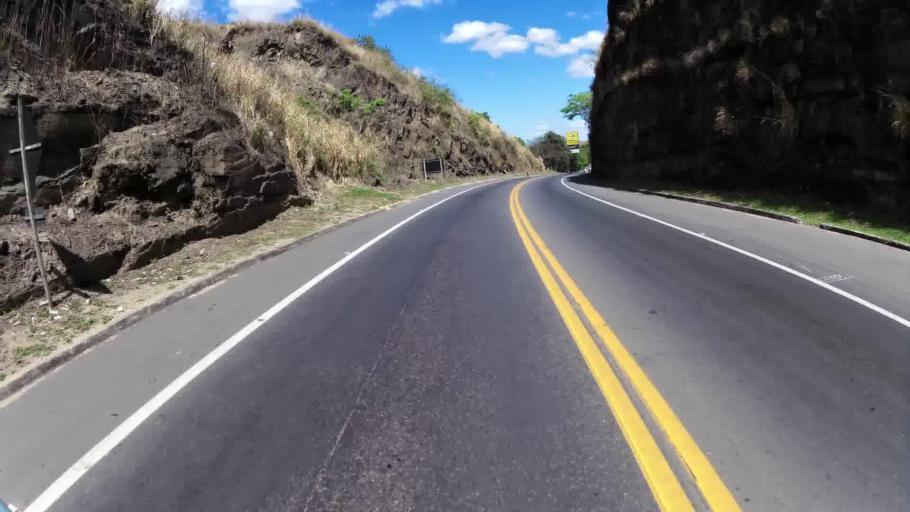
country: BR
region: Minas Gerais
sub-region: Alem Paraiba
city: Alem Paraiba
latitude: -21.8777
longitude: -42.6688
